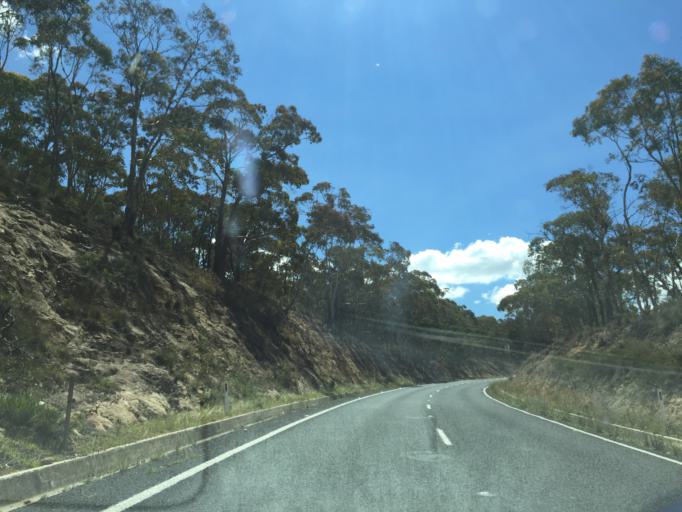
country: AU
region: New South Wales
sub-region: Lithgow
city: Lithgow
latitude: -33.4294
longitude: 150.1059
